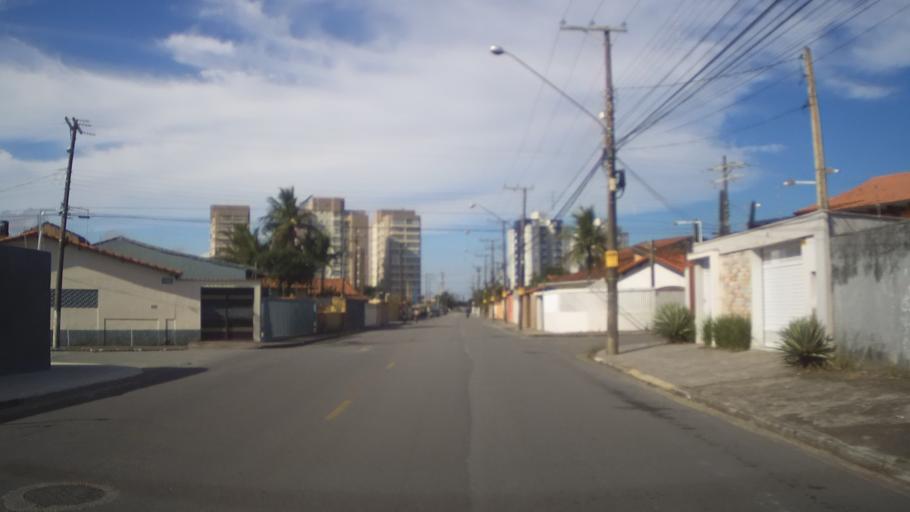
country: BR
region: Sao Paulo
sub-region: Itanhaem
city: Itanhaem
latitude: -24.1757
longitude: -46.7731
